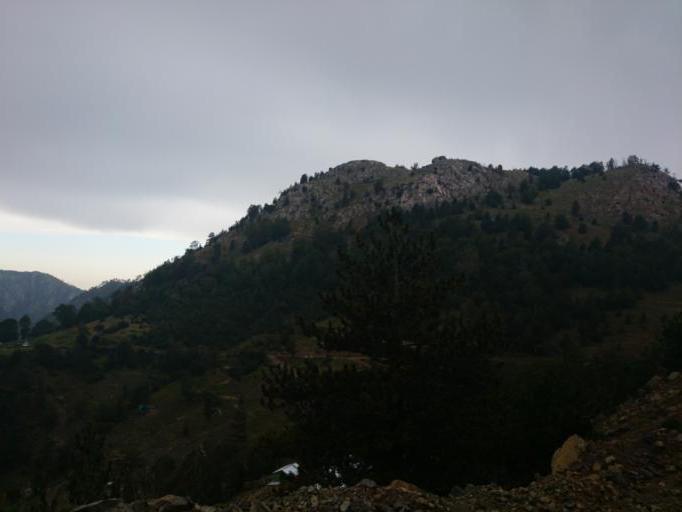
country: AL
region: Lezhe
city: Kurbnesh
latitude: 41.7864
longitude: 20.1517
